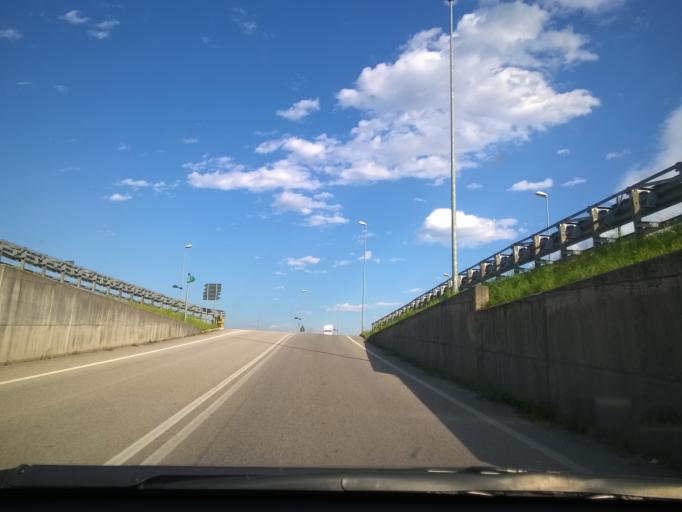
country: IT
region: Veneto
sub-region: Provincia di Treviso
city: Lancenigo-Villorba
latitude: 45.7447
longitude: 12.2507
